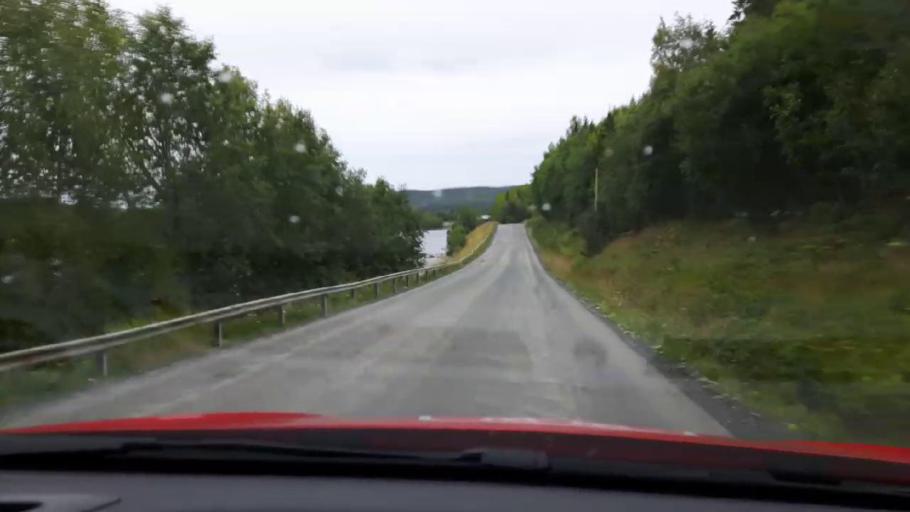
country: SE
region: Jaemtland
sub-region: Are Kommun
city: Jarpen
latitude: 63.4131
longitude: 13.3565
